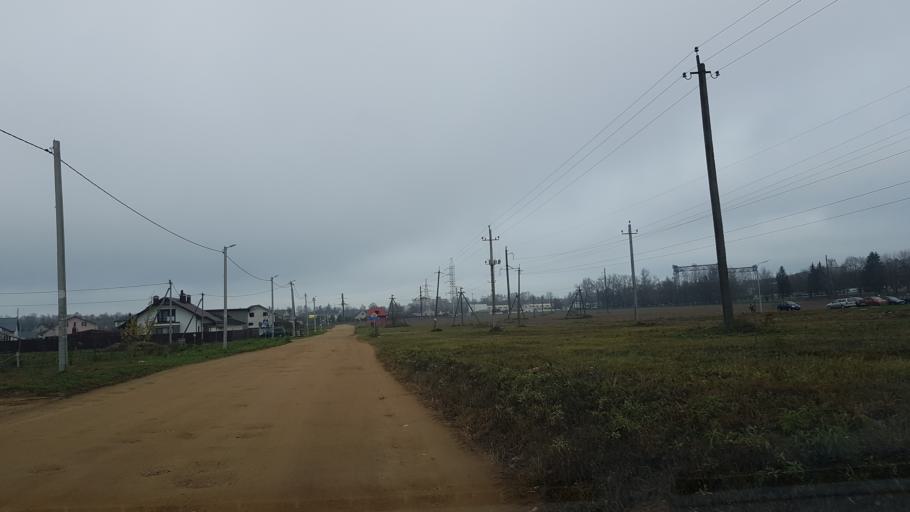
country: BY
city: Fanipol
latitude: 53.7317
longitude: 27.3288
